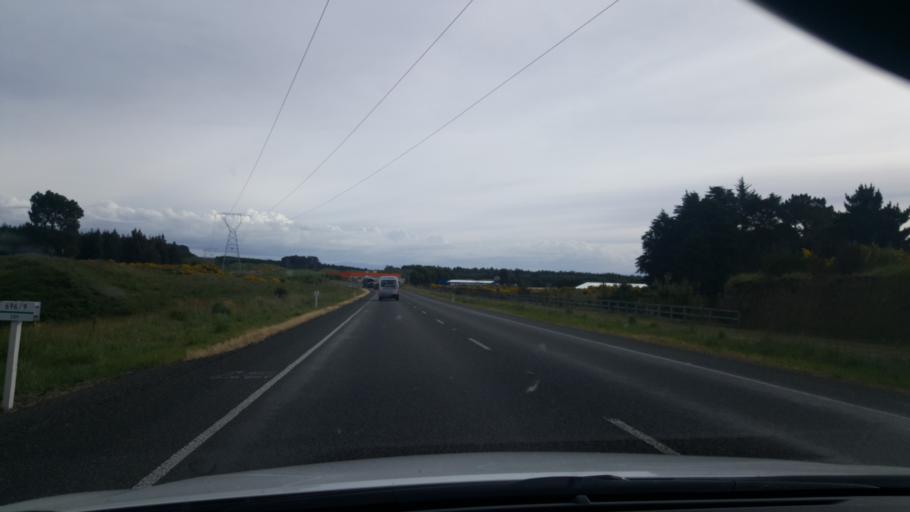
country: NZ
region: Waikato
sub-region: Taupo District
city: Taupo
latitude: -38.6970
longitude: 176.1129
